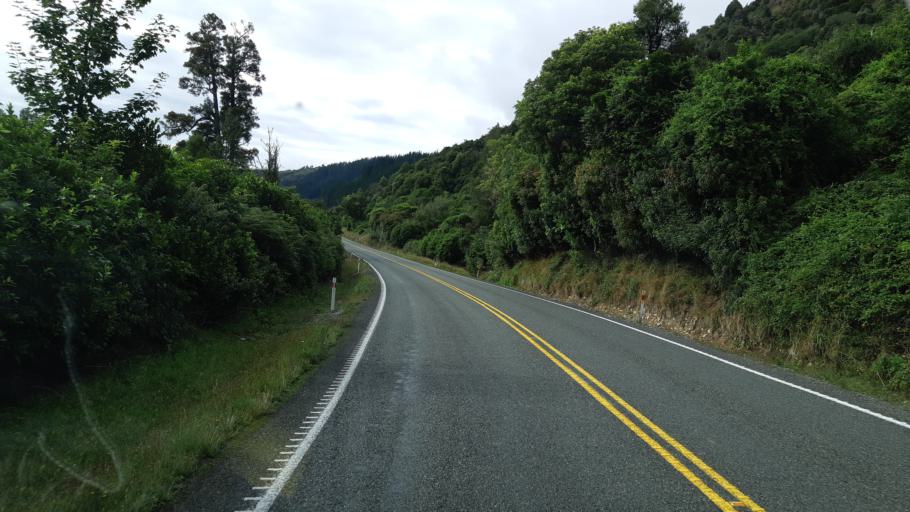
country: NZ
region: West Coast
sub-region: Buller District
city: Westport
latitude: -41.7754
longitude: 172.2407
